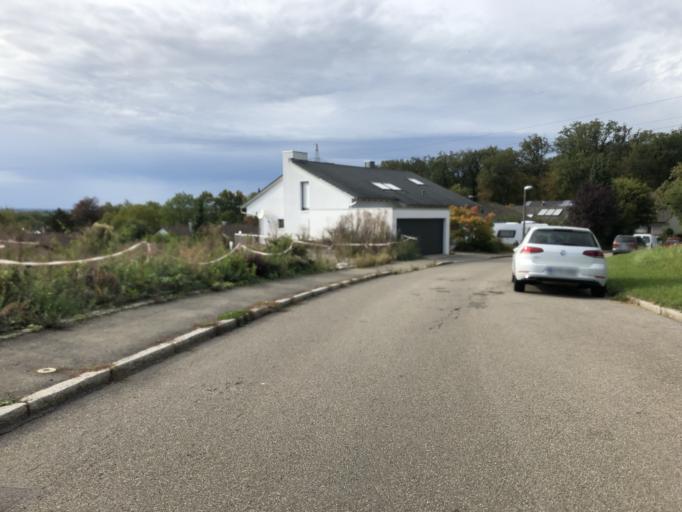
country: DE
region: Baden-Wuerttemberg
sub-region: Regierungsbezirk Stuttgart
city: Sindelfingen
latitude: 48.7180
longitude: 8.9954
